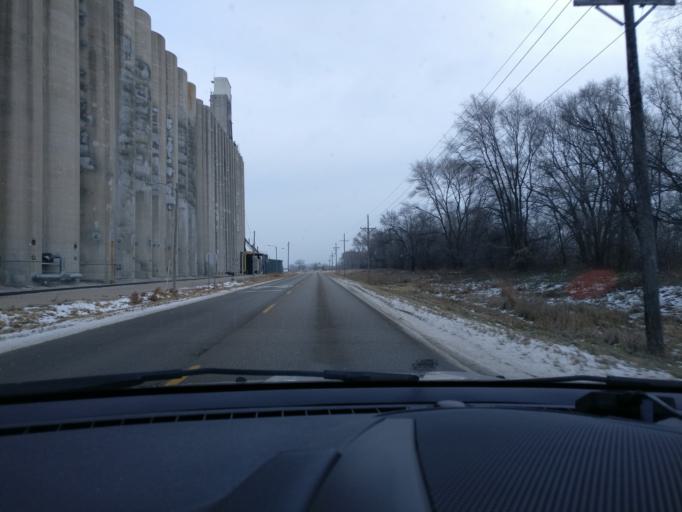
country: US
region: Nebraska
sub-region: Dodge County
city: Fremont
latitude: 41.4476
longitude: -96.5564
